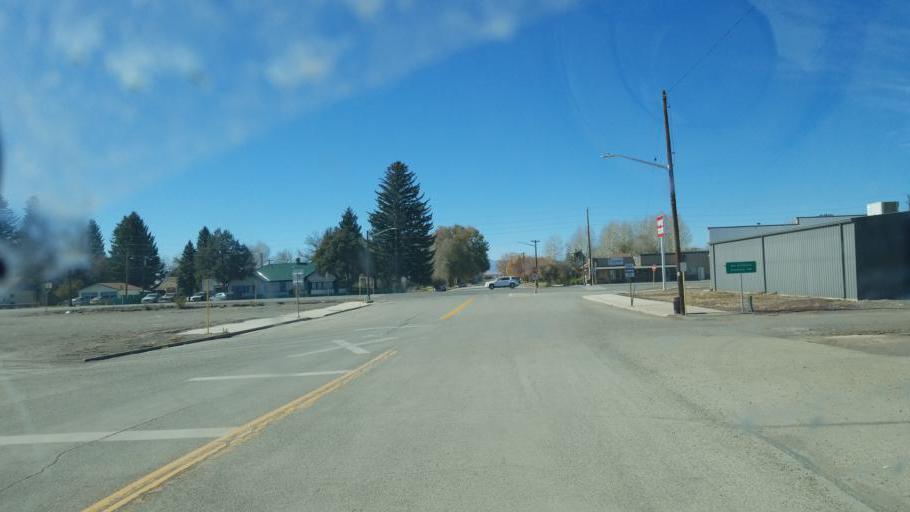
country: US
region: Colorado
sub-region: Conejos County
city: Conejos
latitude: 37.2750
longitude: -105.9607
